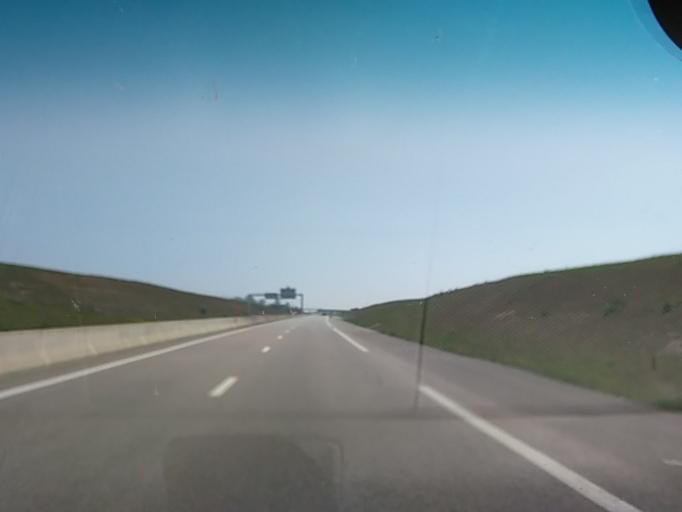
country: FR
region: Lower Normandy
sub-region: Departement de l'Orne
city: Argentan
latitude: 48.6888
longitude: 0.0066
